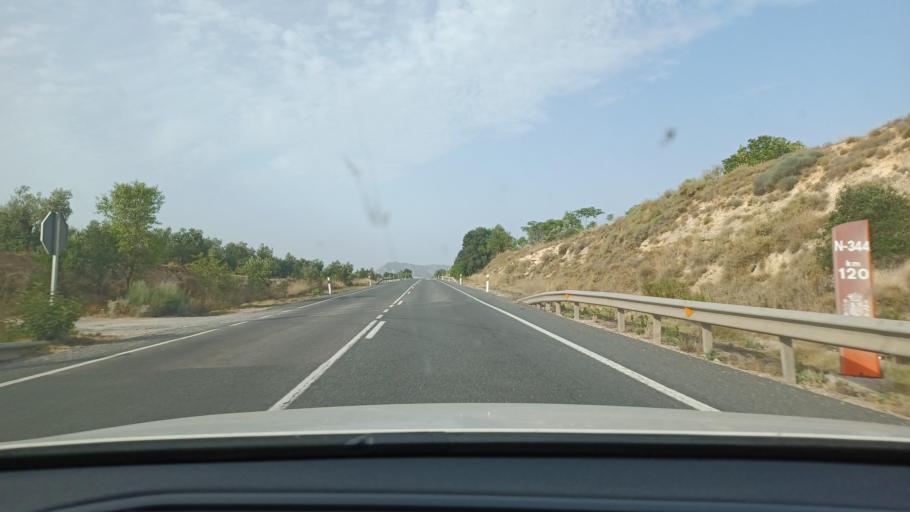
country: ES
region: Castille-La Mancha
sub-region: Provincia de Albacete
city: Caudete
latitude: 38.7406
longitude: -0.9295
